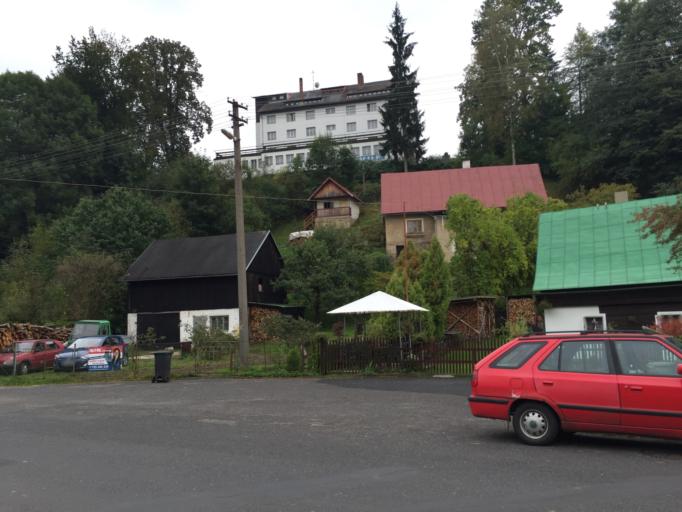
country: CZ
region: Ustecky
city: Ceska Kamenice
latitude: 50.8523
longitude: 14.3948
